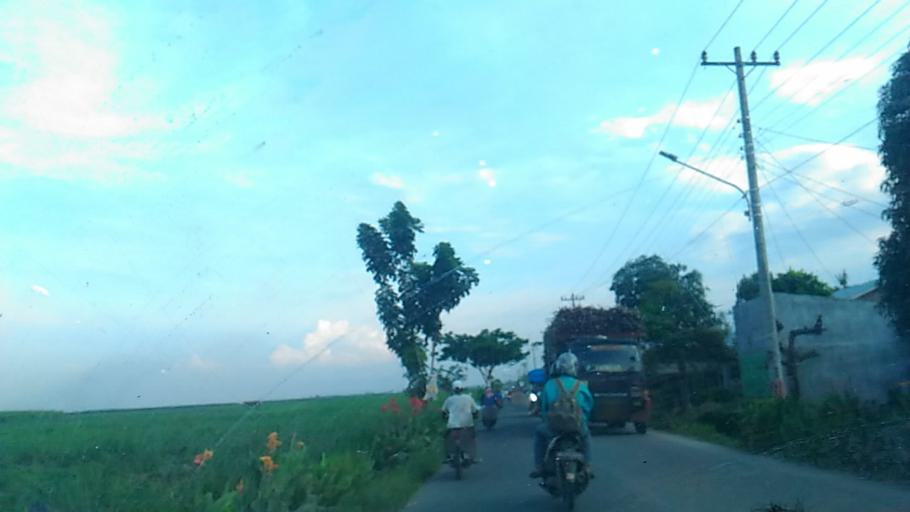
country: ID
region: North Sumatra
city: Labuhan Deli
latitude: 3.6967
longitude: 98.5980
